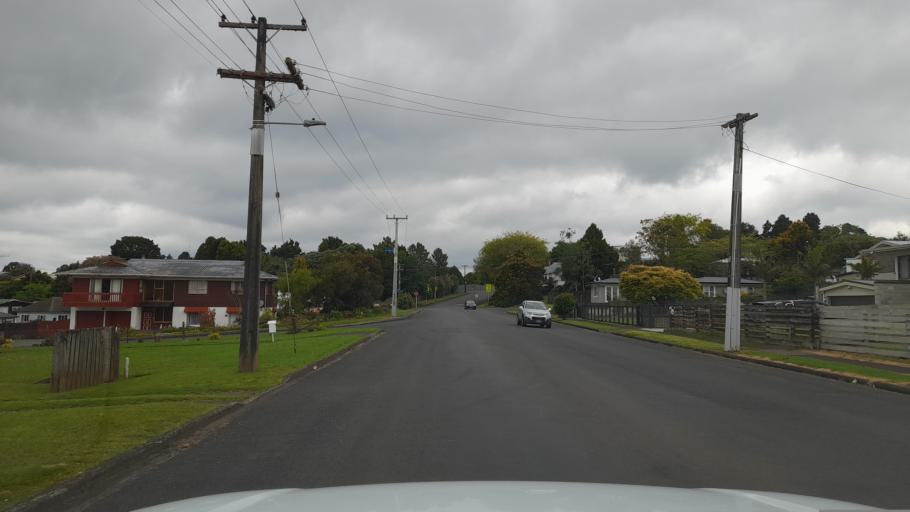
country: NZ
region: Northland
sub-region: Far North District
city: Waimate North
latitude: -35.4051
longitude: 173.7890
